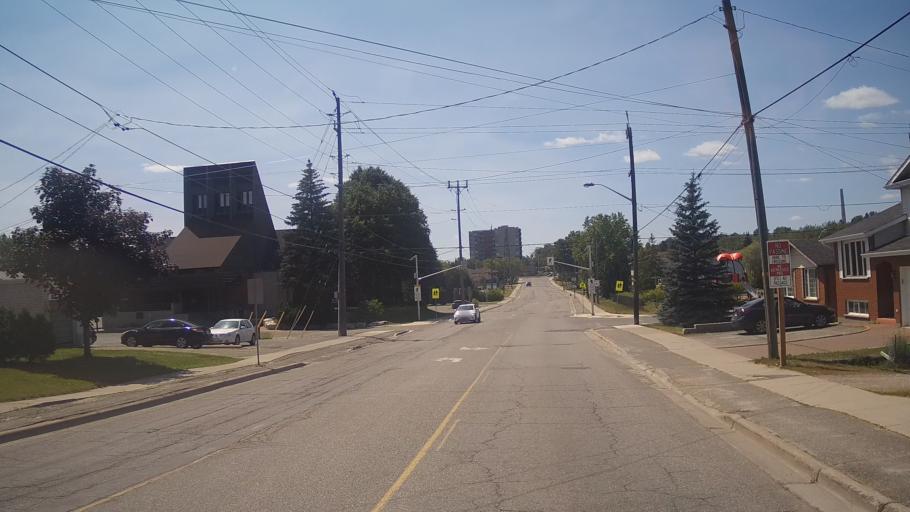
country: CA
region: Ontario
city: Greater Sudbury
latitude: 46.4640
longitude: -81.0024
